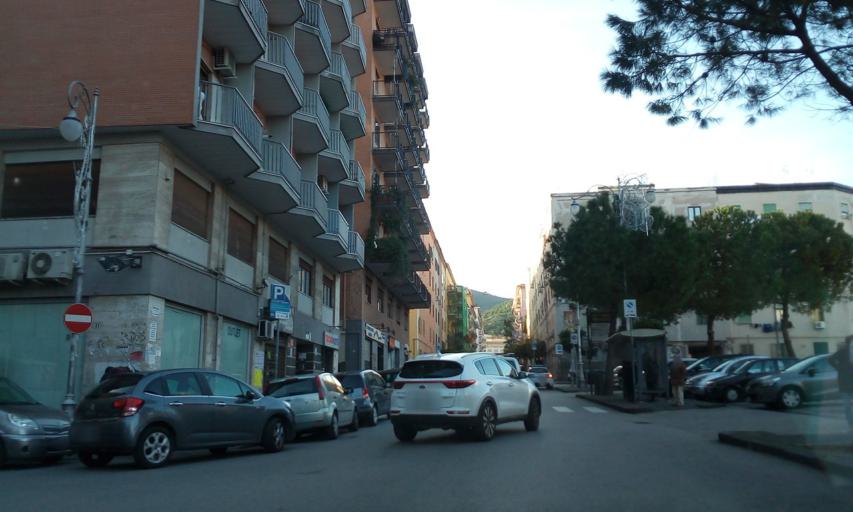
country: IT
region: Campania
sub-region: Provincia di Salerno
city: Capezzano Inferiore
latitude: 40.6798
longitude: 14.7702
